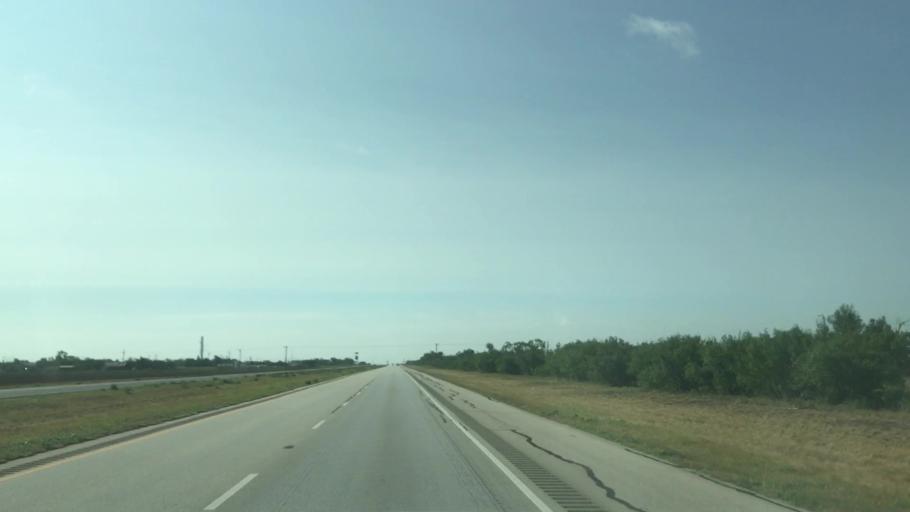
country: US
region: Texas
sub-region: Scurry County
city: Snyder
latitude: 32.6439
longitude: -100.7712
